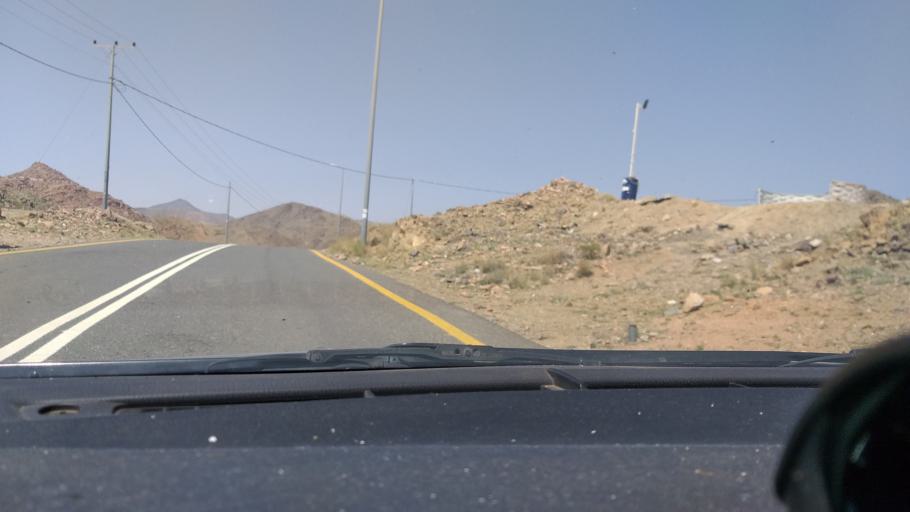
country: SA
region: Makkah
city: Ash Shafa
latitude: 21.1588
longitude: 40.3693
